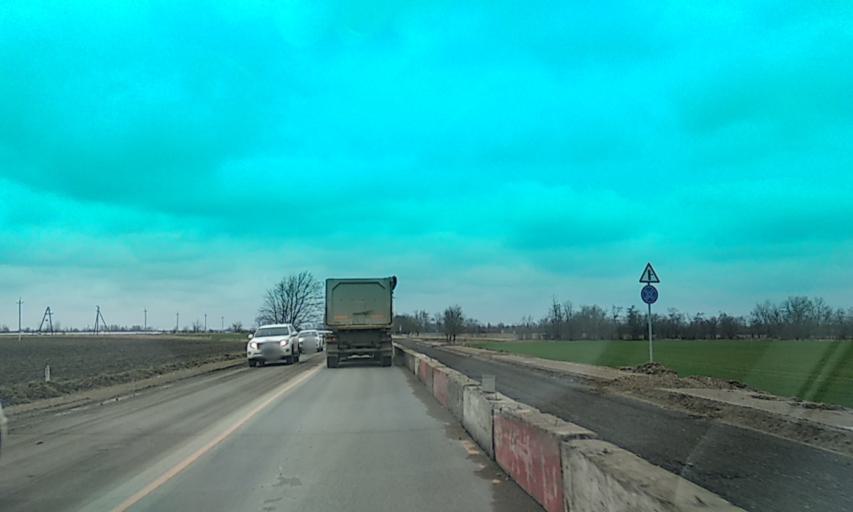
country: RU
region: Adygeya
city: Beloye
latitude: 45.0175
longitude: 39.6925
